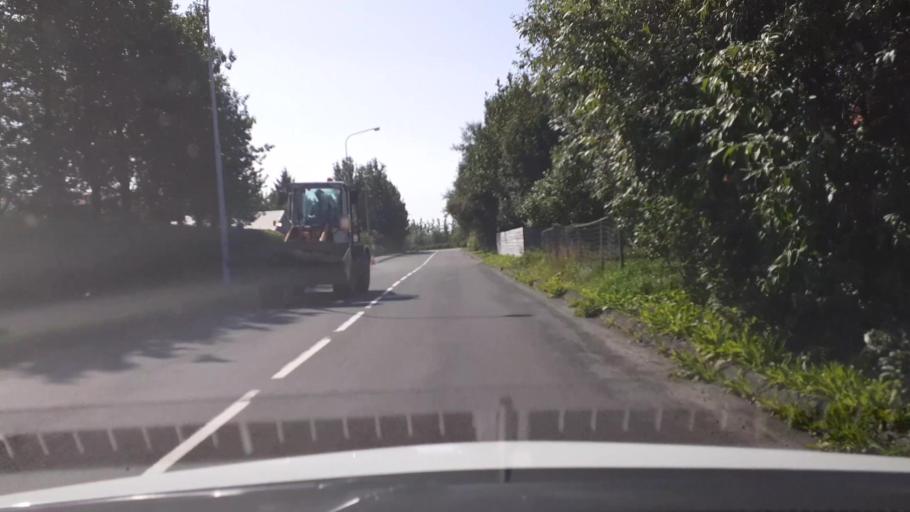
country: IS
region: South
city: Selfoss
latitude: 63.9306
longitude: -21.0104
